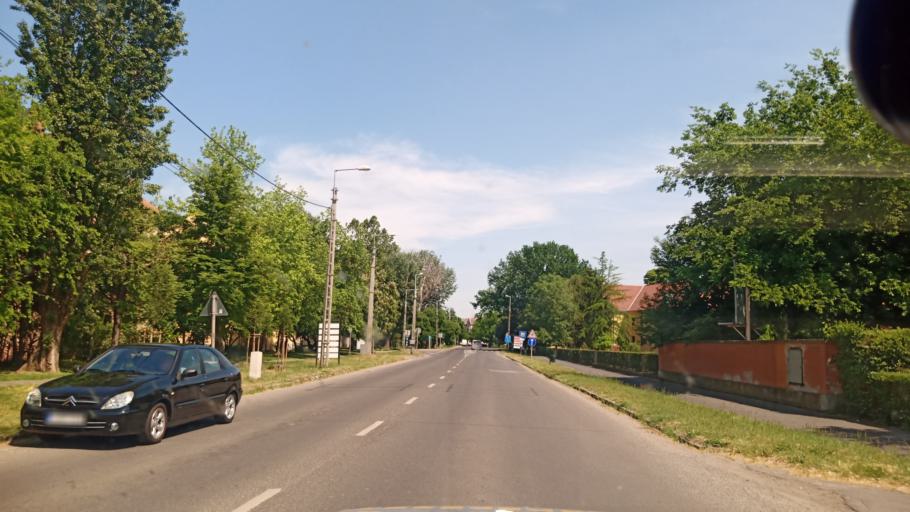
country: HU
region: Bekes
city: Oroshaza
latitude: 46.5573
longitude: 20.6579
